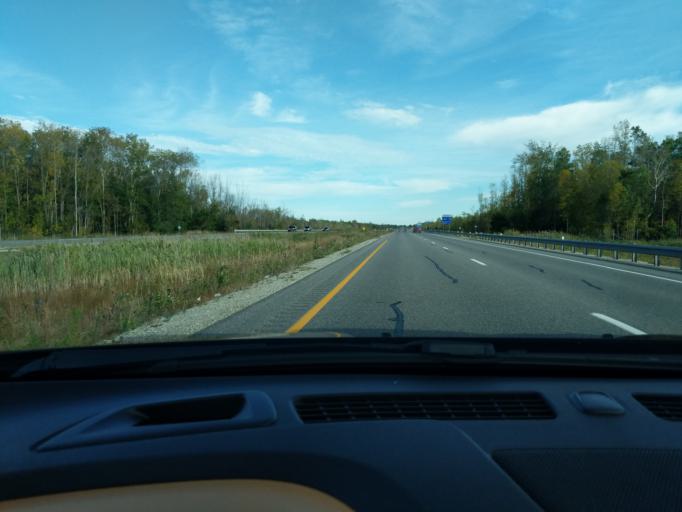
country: CA
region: Ontario
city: Collingwood
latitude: 44.4669
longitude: -80.1310
